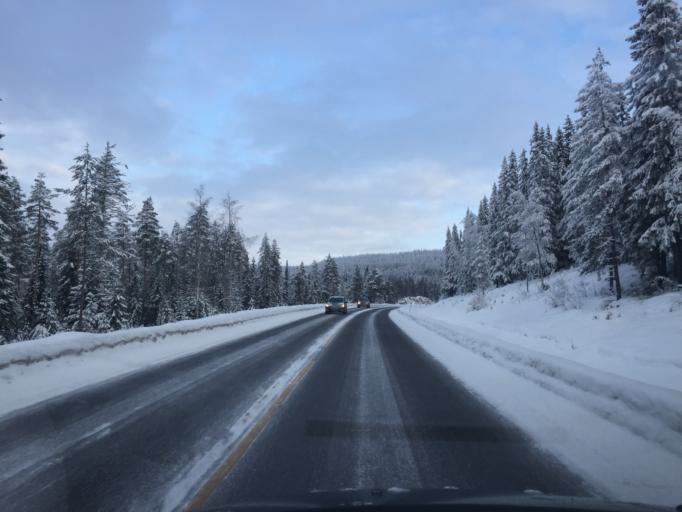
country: NO
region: Hedmark
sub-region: Elverum
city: Elverum
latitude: 61.0423
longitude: 11.8732
